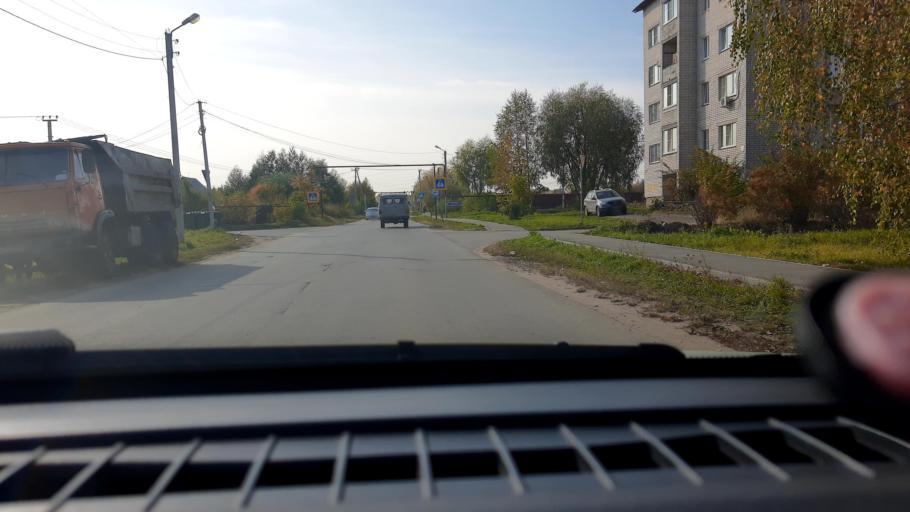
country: RU
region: Nizjnij Novgorod
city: Afonino
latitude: 56.2076
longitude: 44.0991
